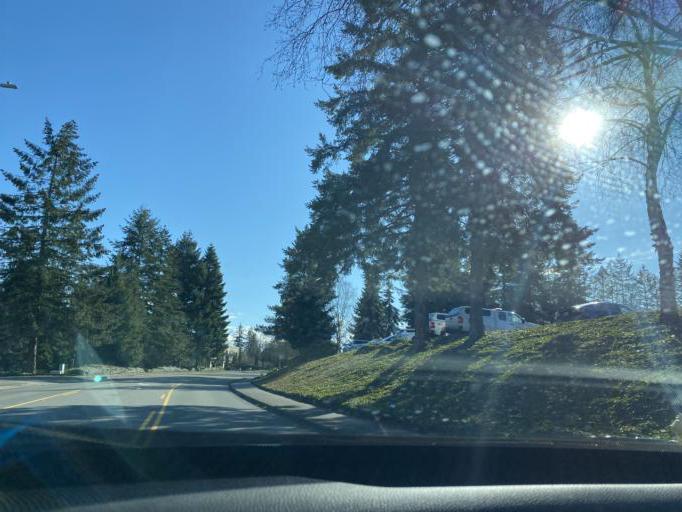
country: US
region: Washington
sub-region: King County
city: Federal Way
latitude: 47.3040
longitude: -122.3214
